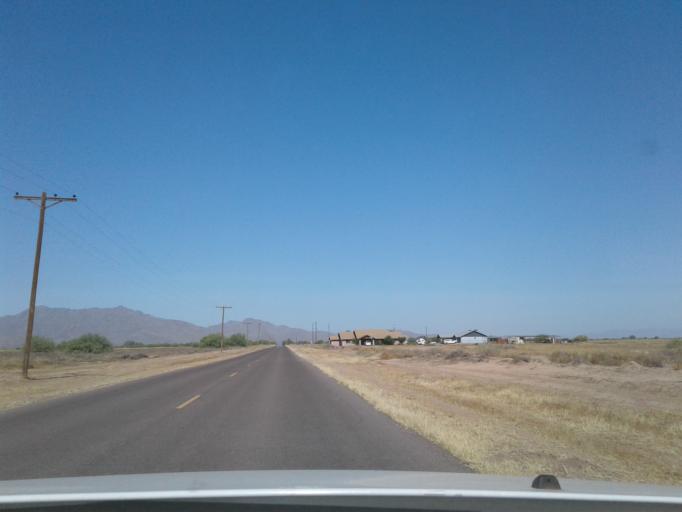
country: US
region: Arizona
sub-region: Maricopa County
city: Laveen
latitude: 33.3340
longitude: -112.1883
